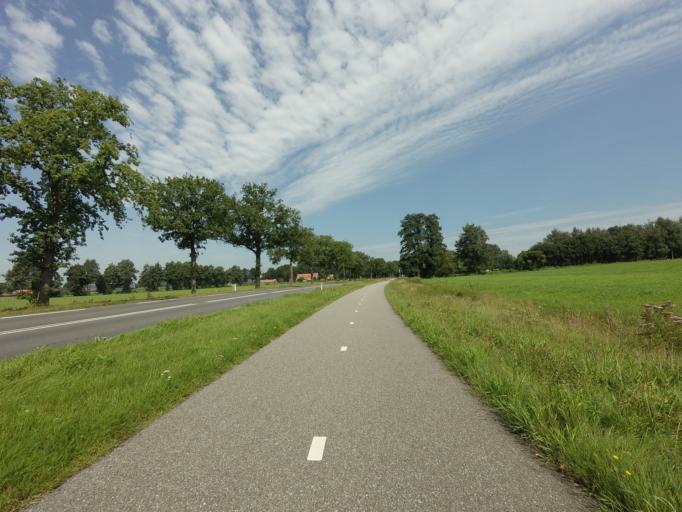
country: NL
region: Overijssel
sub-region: Gemeente Hof van Twente
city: Delden
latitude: 52.2387
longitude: 6.6915
